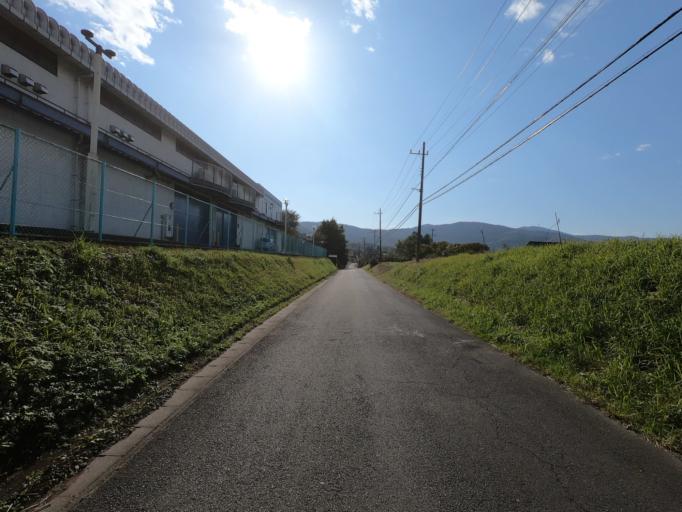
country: JP
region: Ibaraki
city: Tsukuba
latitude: 36.1904
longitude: 140.1809
